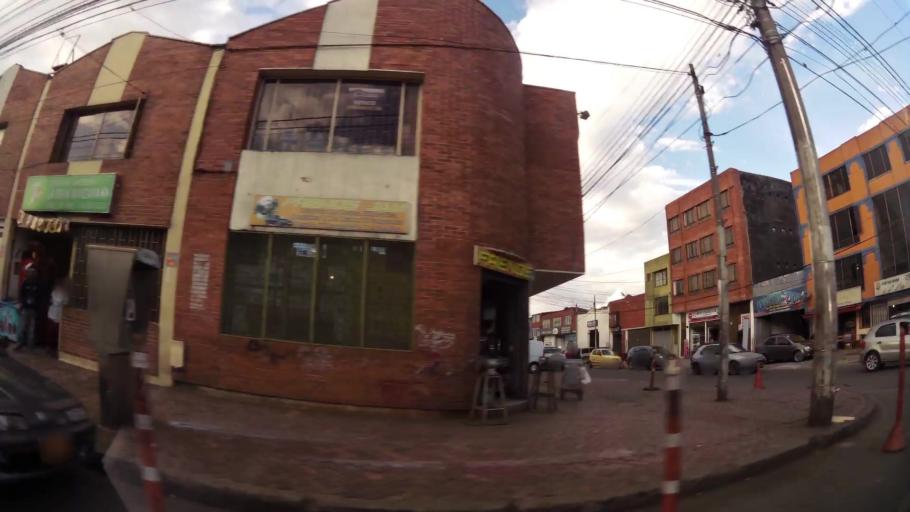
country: CO
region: Bogota D.C.
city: Bogota
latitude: 4.6555
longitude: -74.0766
